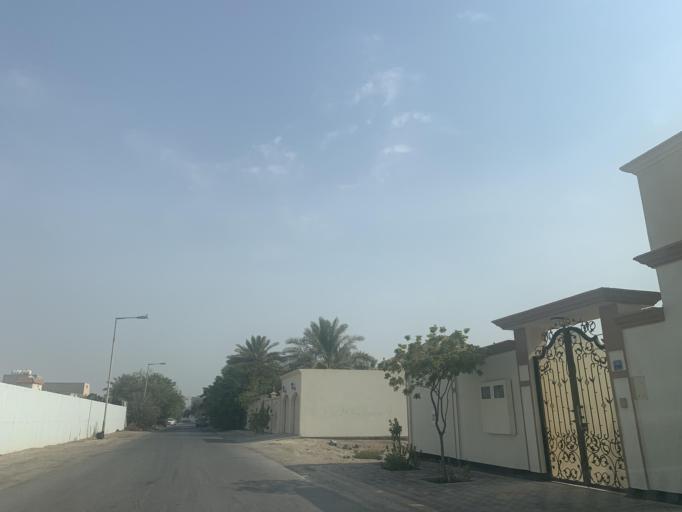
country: BH
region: Manama
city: Jidd Hafs
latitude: 26.2133
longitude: 50.4926
